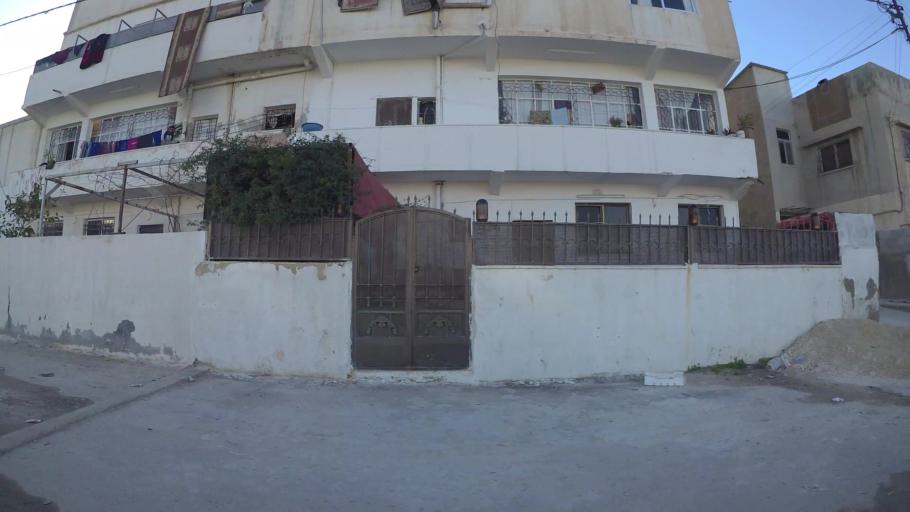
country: JO
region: Amman
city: Al Bunayyat ash Shamaliyah
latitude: 31.9085
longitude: 35.9161
